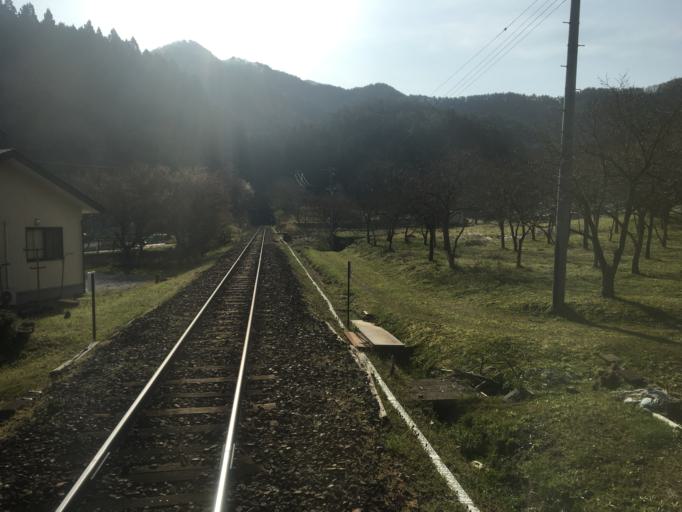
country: JP
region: Iwate
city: Ofunato
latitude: 39.0676
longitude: 141.7444
